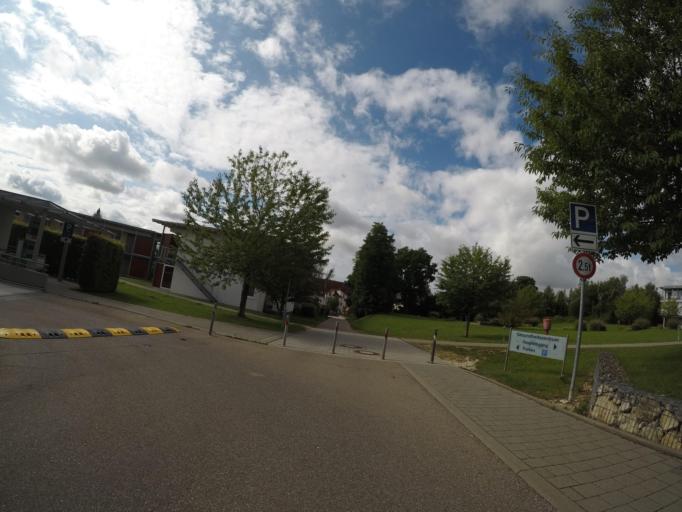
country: DE
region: Baden-Wuerttemberg
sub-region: Tuebingen Region
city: Langenau
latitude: 48.5000
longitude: 10.1175
